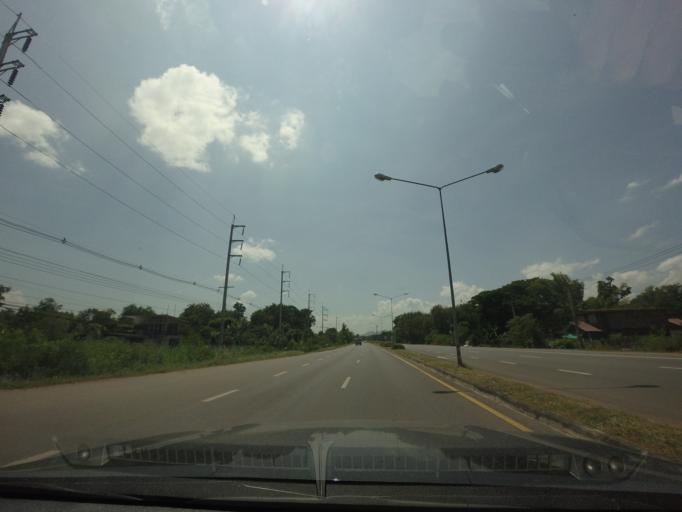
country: TH
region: Phetchabun
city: Lom Sak
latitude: 16.6865
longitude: 101.1649
